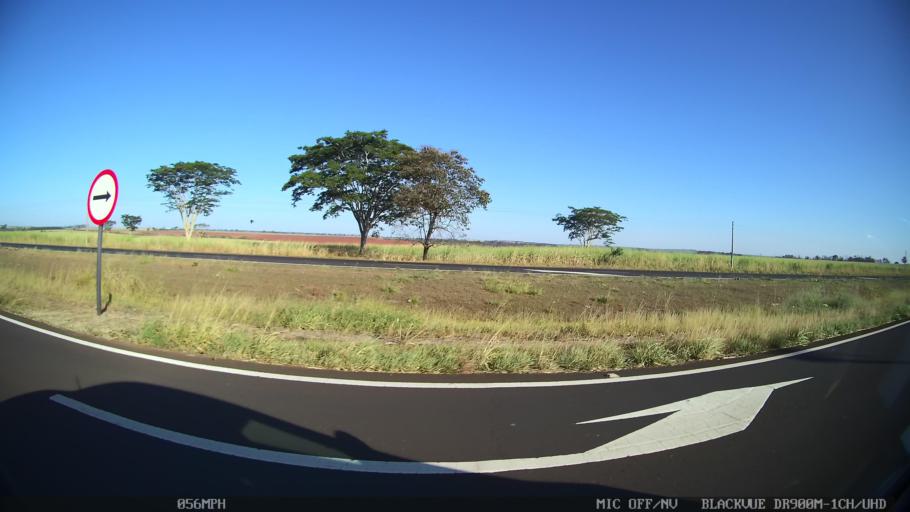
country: BR
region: Sao Paulo
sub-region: Olimpia
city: Olimpia
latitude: -20.7242
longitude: -49.0300
